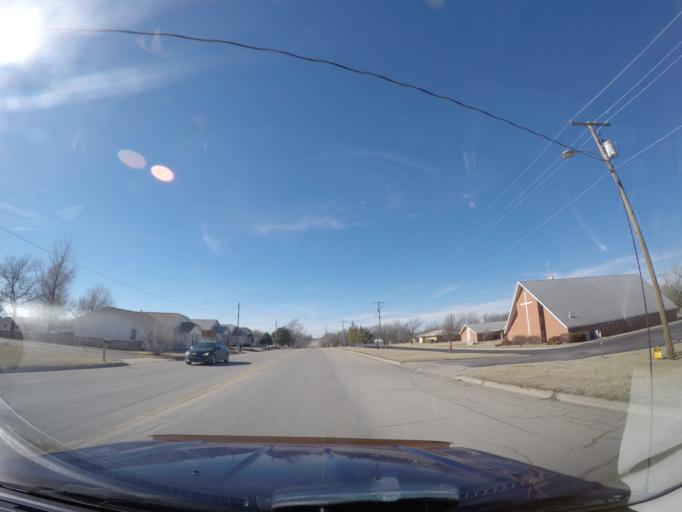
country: US
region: Kansas
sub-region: Dickinson County
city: Herington
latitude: 38.6675
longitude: -96.9326
